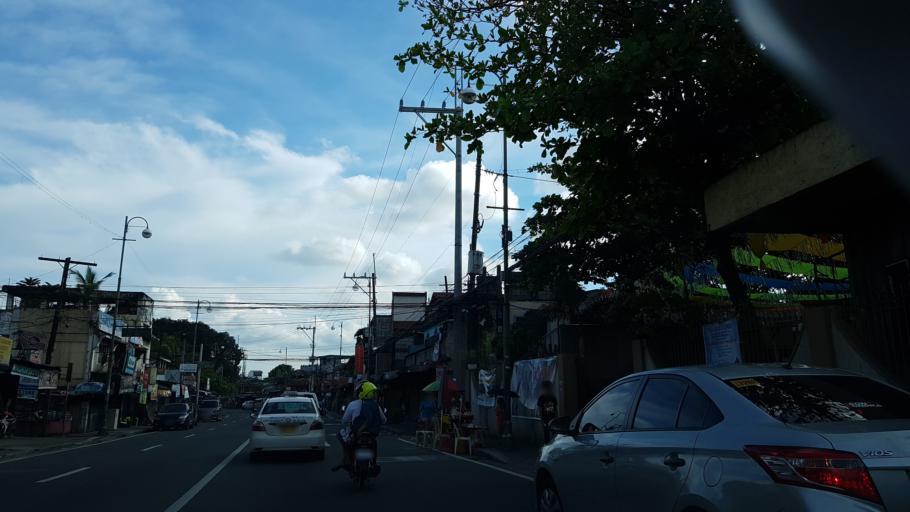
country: PH
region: Calabarzon
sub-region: Province of Rizal
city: Pateros
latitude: 14.5531
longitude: 121.0635
